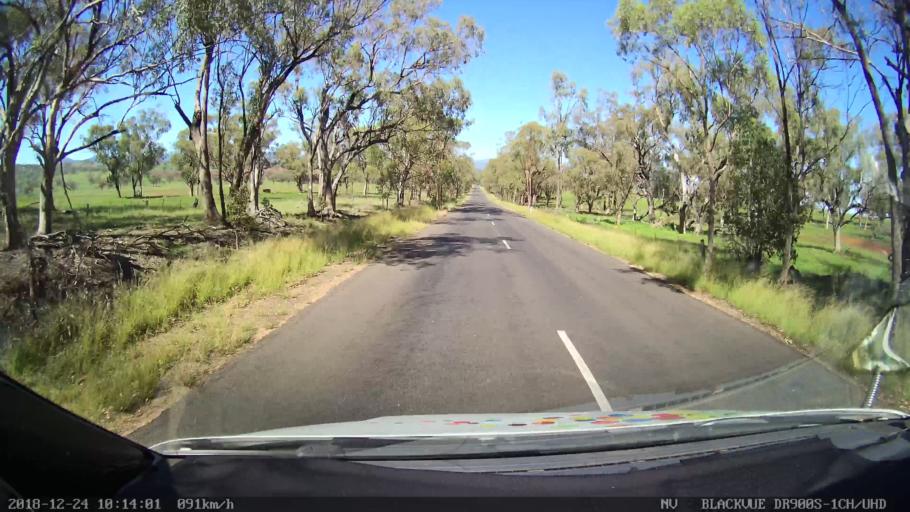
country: AU
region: New South Wales
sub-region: Liverpool Plains
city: Quirindi
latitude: -31.6945
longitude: 150.6340
